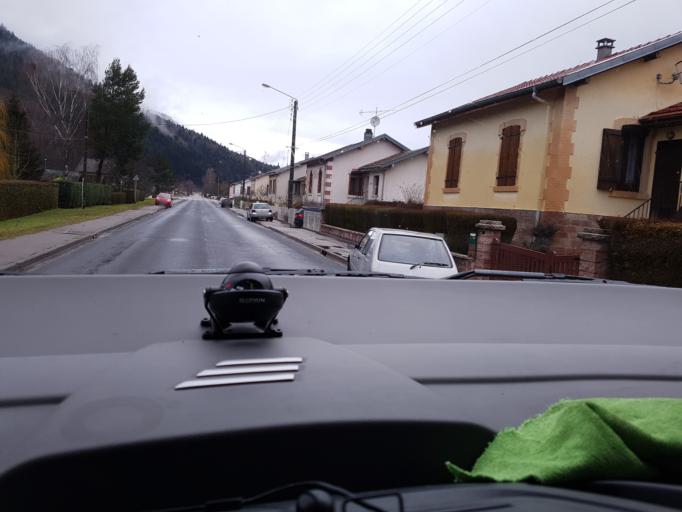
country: FR
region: Lorraine
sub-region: Departement des Vosges
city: Saint-Die-des-Vosges
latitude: 48.2901
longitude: 6.9245
